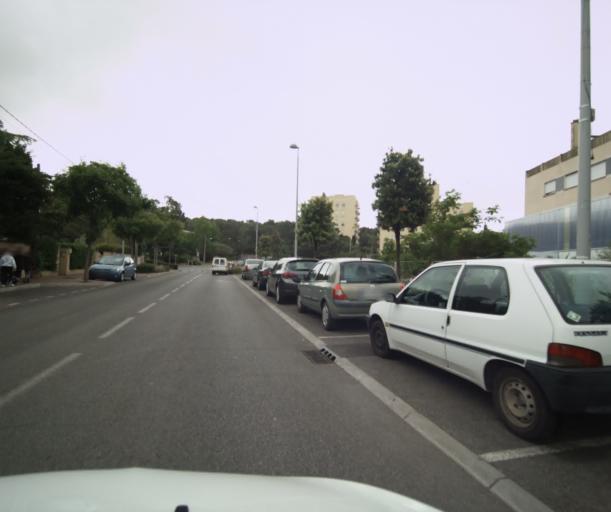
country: FR
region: Provence-Alpes-Cote d'Azur
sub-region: Departement du Var
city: La Valette-du-Var
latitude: 43.1307
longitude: 5.9907
